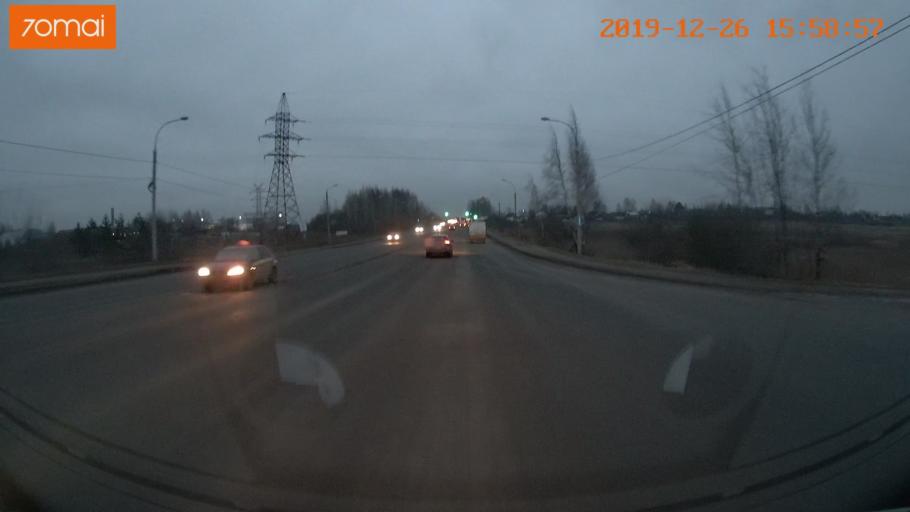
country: RU
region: Jaroslavl
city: Rybinsk
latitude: 58.0351
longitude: 38.8003
